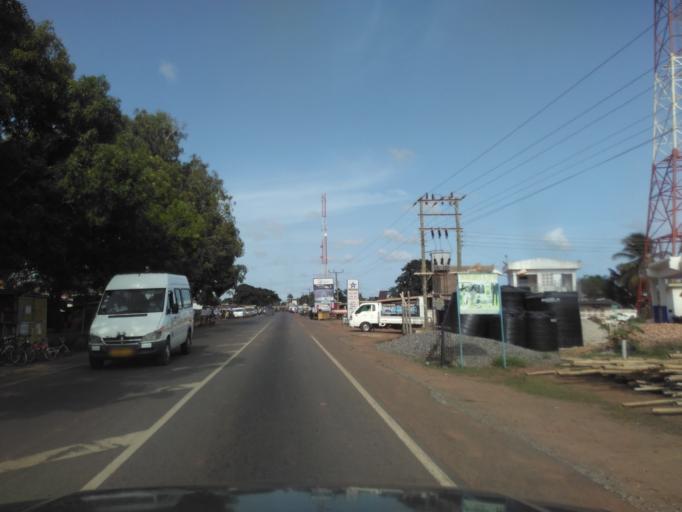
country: GH
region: Volta
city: Anloga
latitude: 5.8964
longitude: 0.5180
